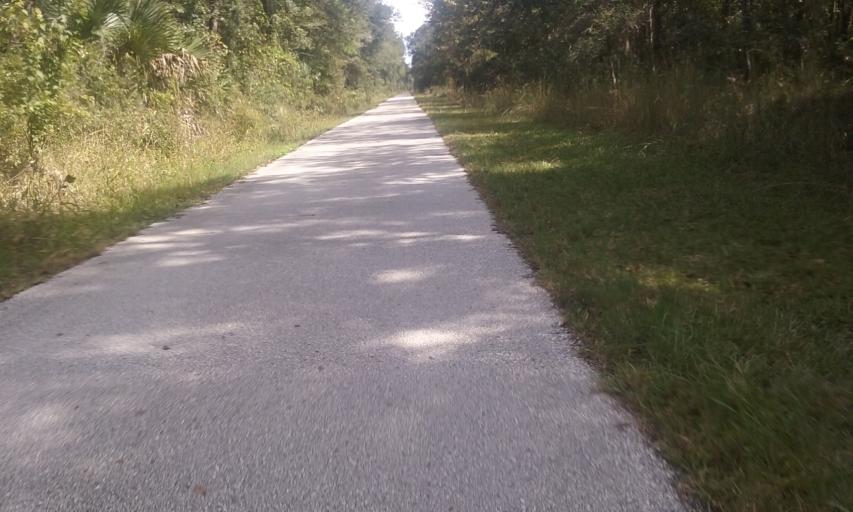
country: US
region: Florida
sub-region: Alachua County
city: Hawthorne
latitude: 29.5941
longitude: -82.1718
